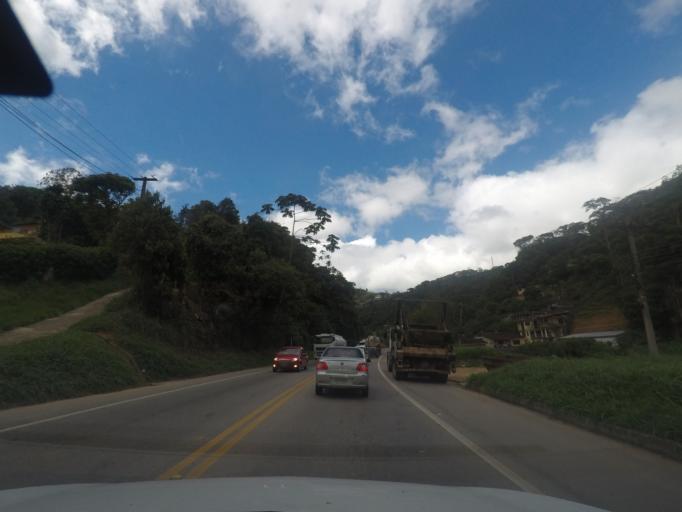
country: BR
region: Rio de Janeiro
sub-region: Teresopolis
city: Teresopolis
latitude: -22.3954
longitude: -42.9532
